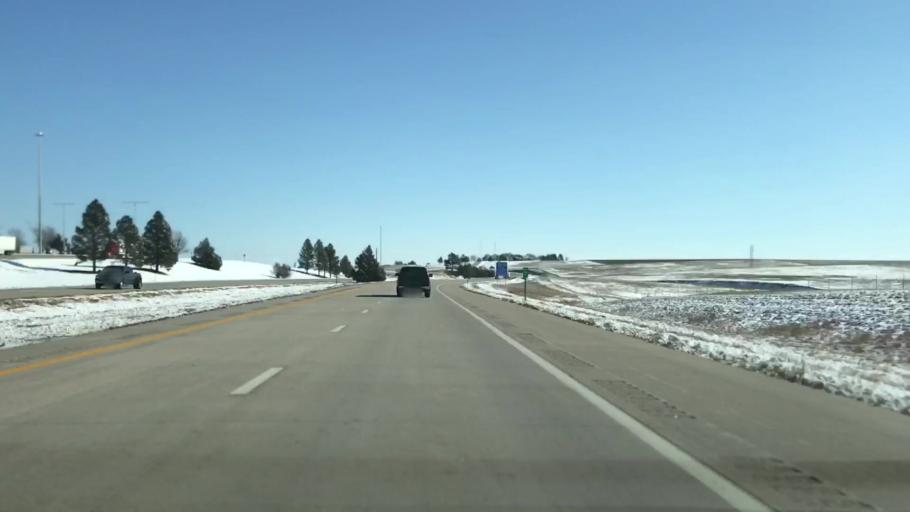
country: US
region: Kansas
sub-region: Sherman County
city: Goodland
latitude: 39.3291
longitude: -101.9184
